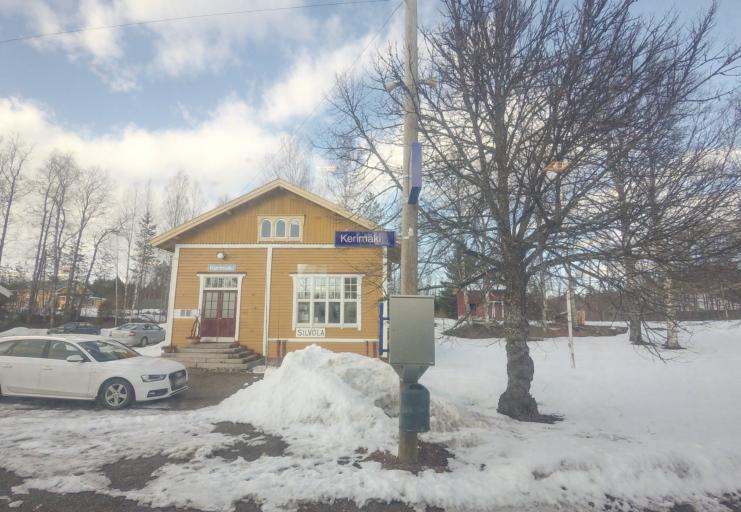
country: FI
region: Southern Savonia
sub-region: Savonlinna
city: Kerimaeki
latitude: 61.8614
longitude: 29.1140
